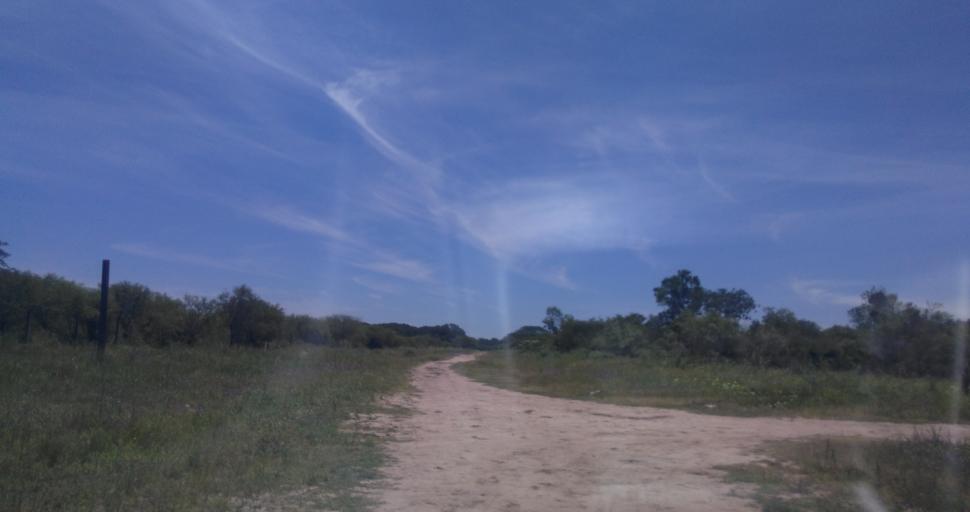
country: AR
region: Chaco
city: Fontana
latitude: -27.4292
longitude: -59.0495
